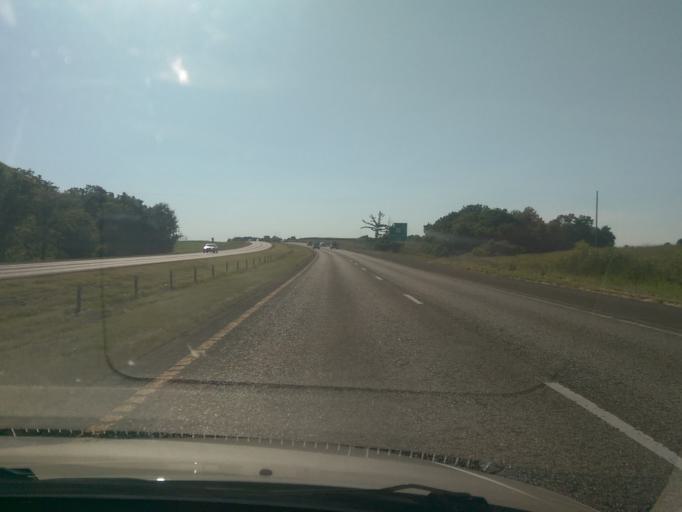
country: US
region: Missouri
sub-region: Lafayette County
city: Concordia
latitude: 38.9913
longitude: -93.6485
